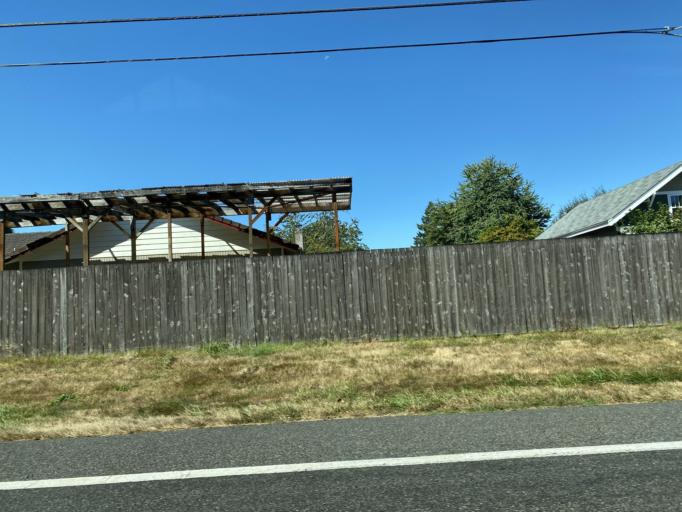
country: US
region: Washington
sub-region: Thurston County
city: Olympia
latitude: 47.0220
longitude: -122.8652
